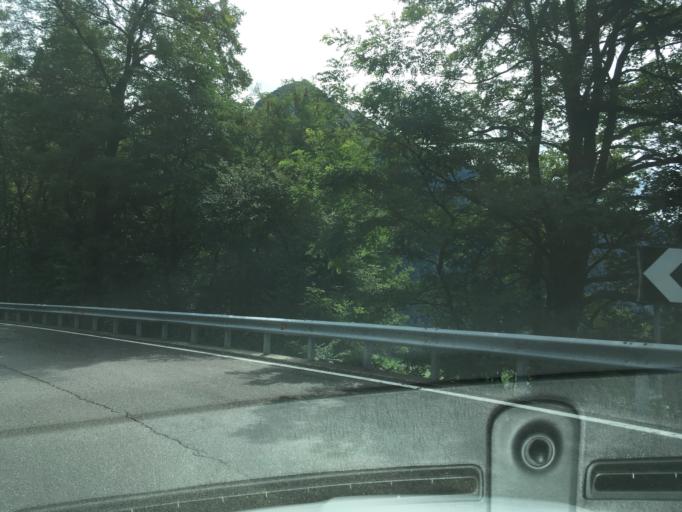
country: IT
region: Trentino-Alto Adige
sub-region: Bolzano
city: San Leonardo in Passiria
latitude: 46.8210
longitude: 11.2466
